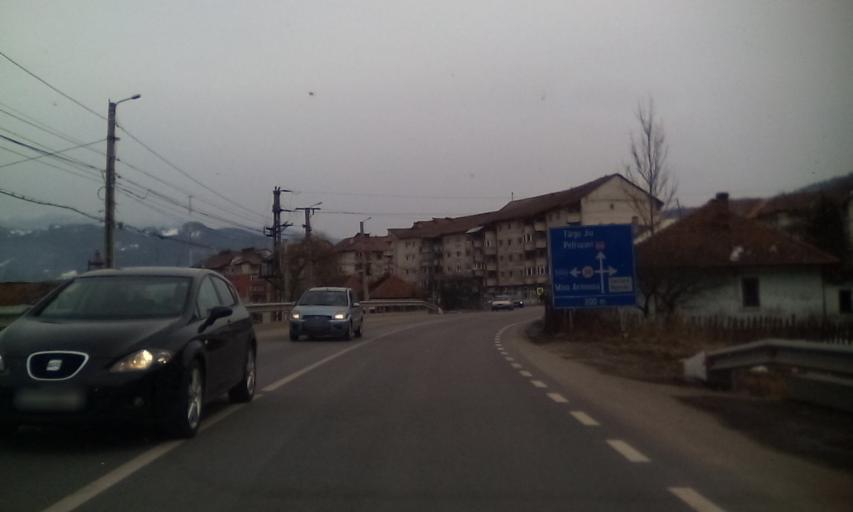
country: RO
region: Hunedoara
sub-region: Comuna Aninoasa
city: Iscroni
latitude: 45.3773
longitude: 23.3328
